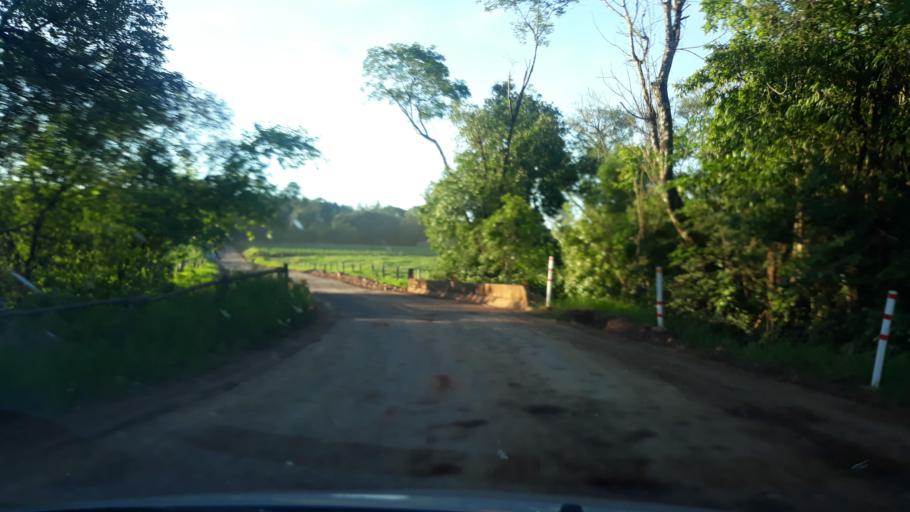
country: AR
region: Misiones
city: Ruiz de Montoya
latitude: -27.0458
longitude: -55.0036
